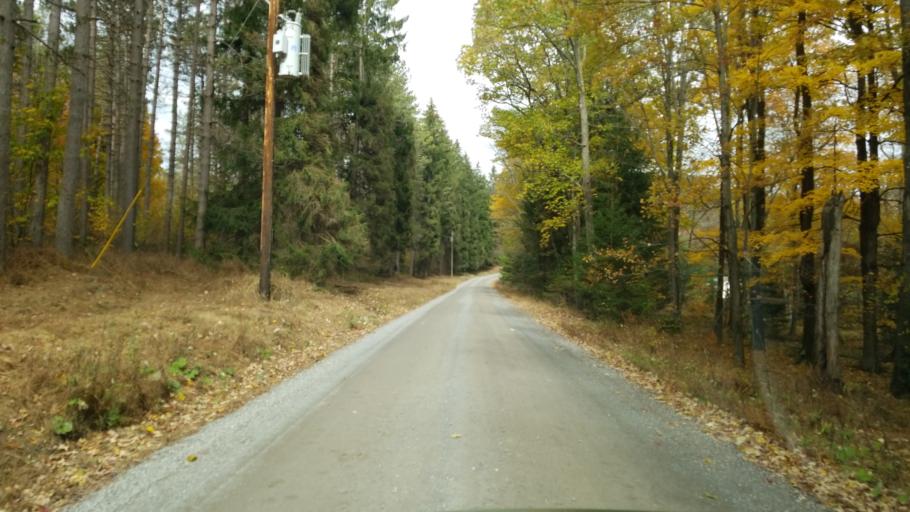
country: US
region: Pennsylvania
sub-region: Clearfield County
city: Clearfield
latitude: 41.1869
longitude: -78.4428
